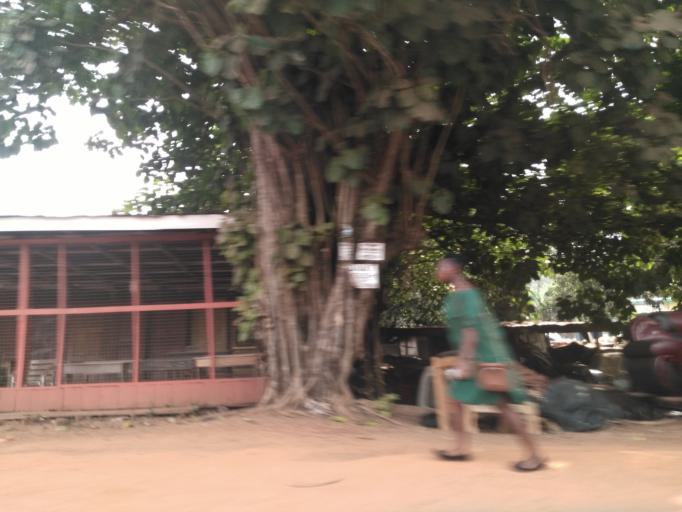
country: GH
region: Ashanti
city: Kumasi
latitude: 6.7090
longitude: -1.6350
